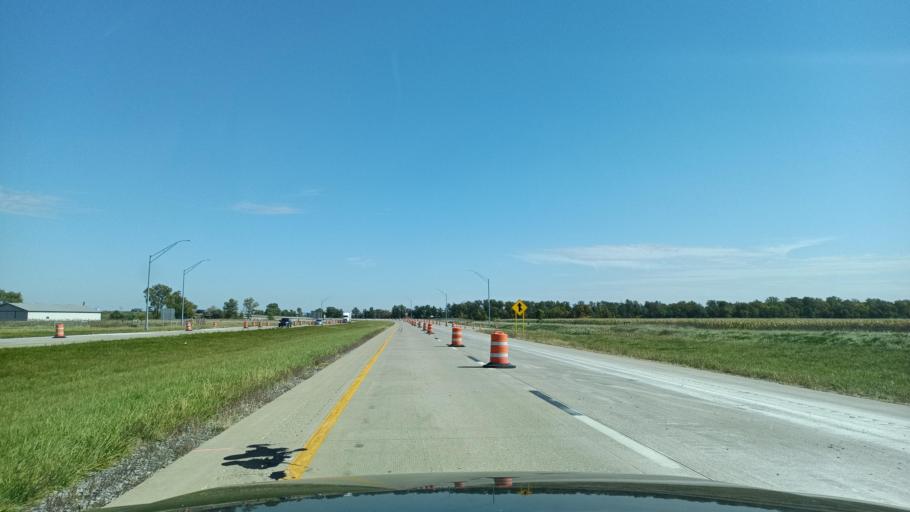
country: US
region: Ohio
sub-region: Paulding County
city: Paulding
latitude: 41.2202
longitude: -84.5798
